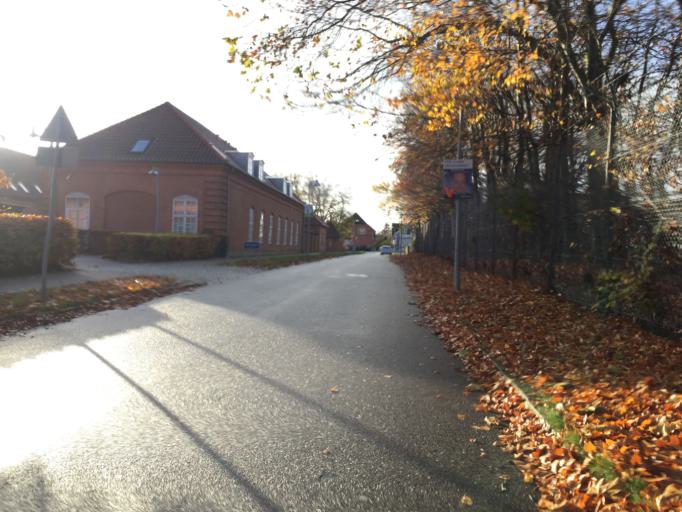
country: DK
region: Zealand
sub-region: Ringsted Kommune
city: Ringsted
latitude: 55.4499
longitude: 11.7940
